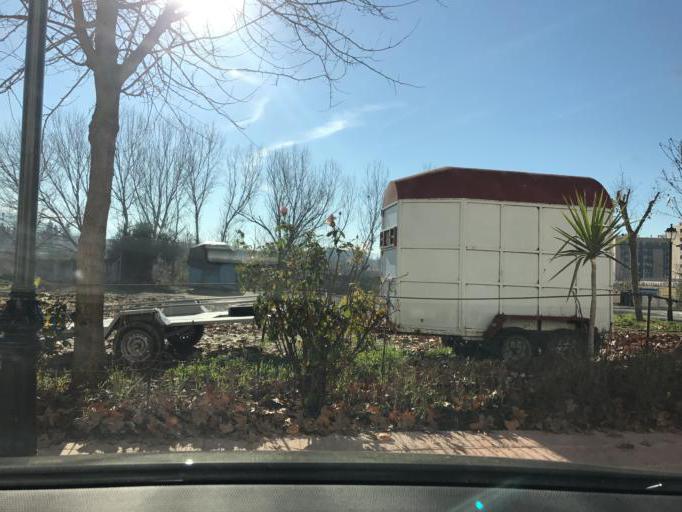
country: ES
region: Andalusia
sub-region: Provincia de Granada
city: Pulianas
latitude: 37.2140
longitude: -3.6077
